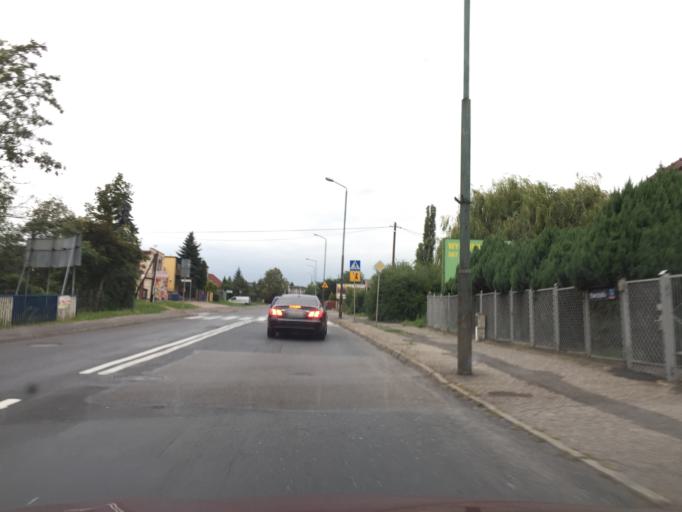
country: PL
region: Greater Poland Voivodeship
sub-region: Kalisz
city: Kalisz
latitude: 51.7729
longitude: 18.0915
